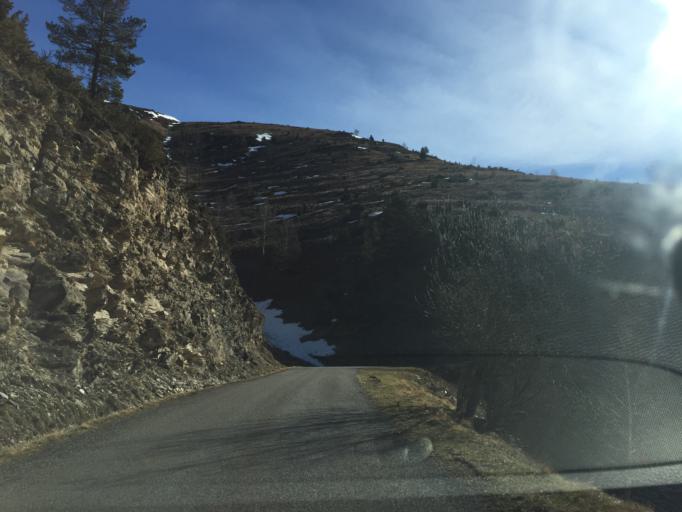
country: FR
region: Midi-Pyrenees
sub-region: Departement des Hautes-Pyrenees
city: Saint-Lary-Soulan
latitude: 42.8143
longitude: 0.3565
